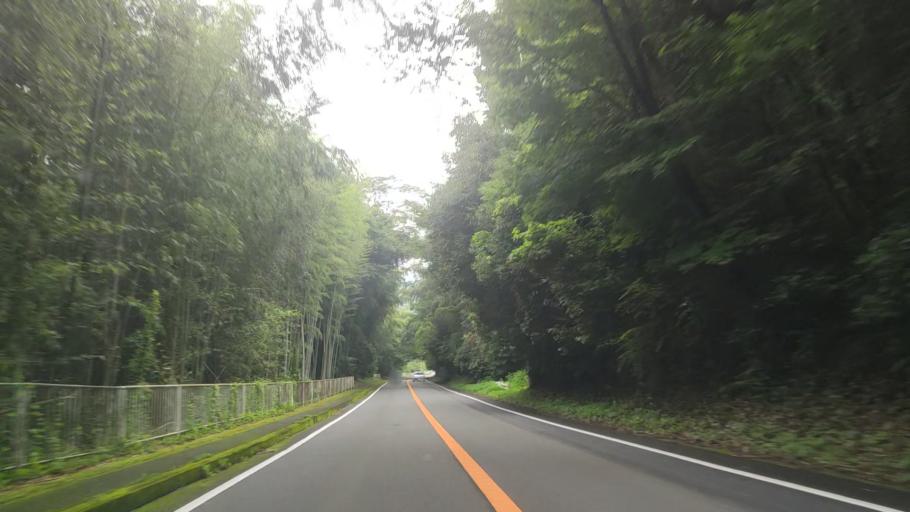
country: JP
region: Shizuoka
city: Fujinomiya
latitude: 35.1971
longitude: 138.5741
